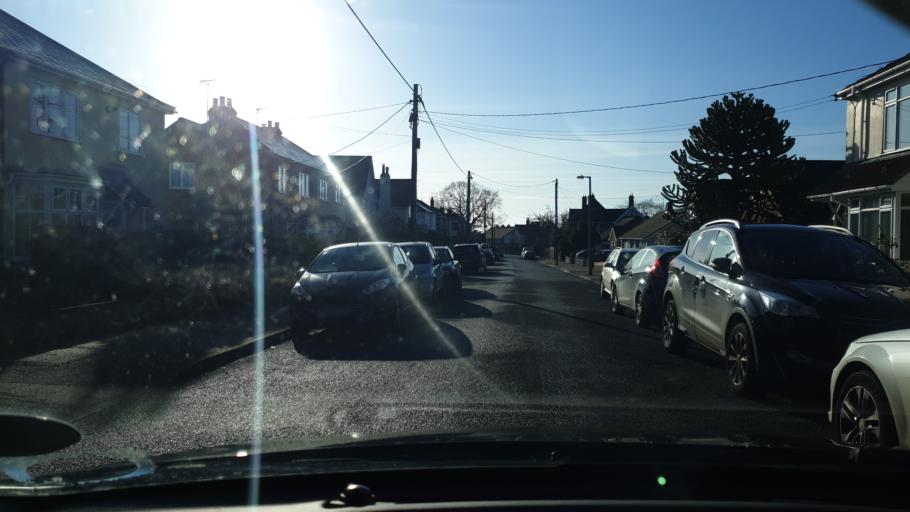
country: GB
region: England
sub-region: Essex
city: Brightlingsea
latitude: 51.8158
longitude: 1.0242
